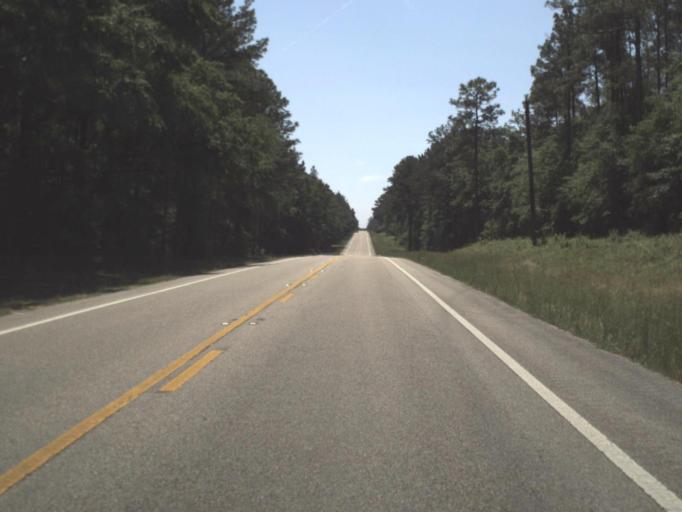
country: US
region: Florida
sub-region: Jackson County
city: Marianna
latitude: 30.6493
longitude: -85.2081
